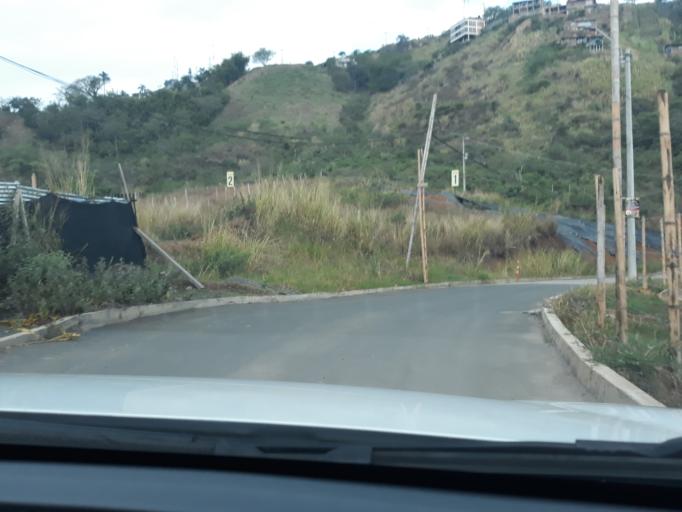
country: CO
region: Valle del Cauca
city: Cali
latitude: 3.4323
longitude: -76.5535
